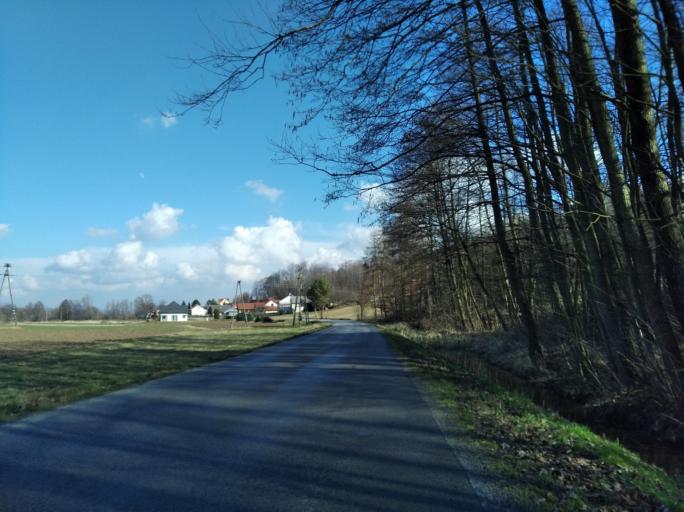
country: PL
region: Subcarpathian Voivodeship
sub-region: Powiat strzyzowski
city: Wisniowa
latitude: 49.8578
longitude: 21.6368
